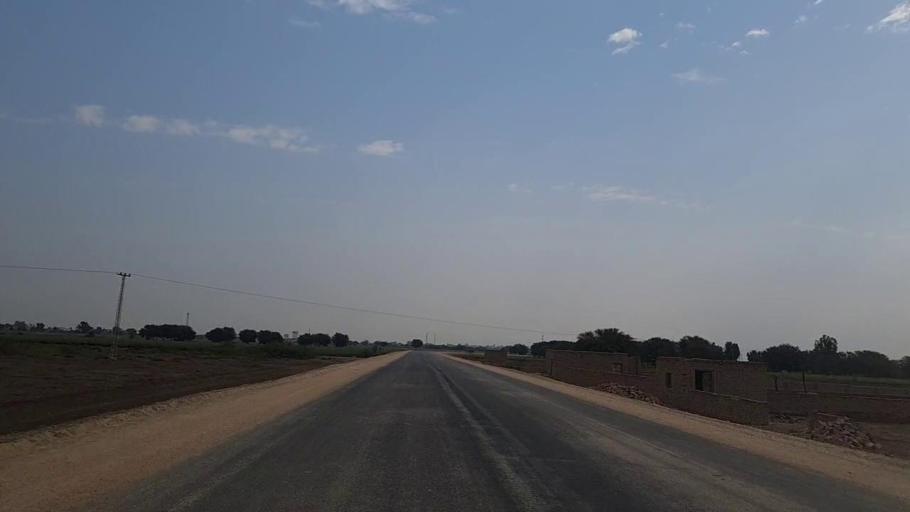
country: PK
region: Sindh
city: Naukot
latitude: 24.9815
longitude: 69.2849
